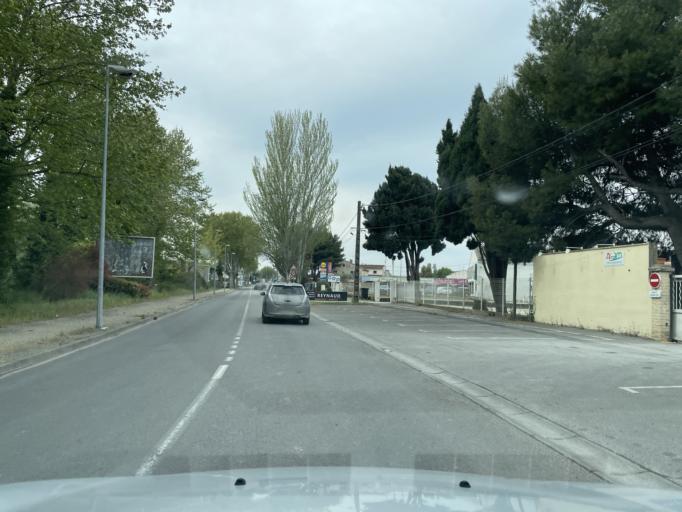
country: FR
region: Provence-Alpes-Cote d'Azur
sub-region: Departement des Bouches-du-Rhone
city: Tarascon
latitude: 43.8131
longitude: 4.6699
